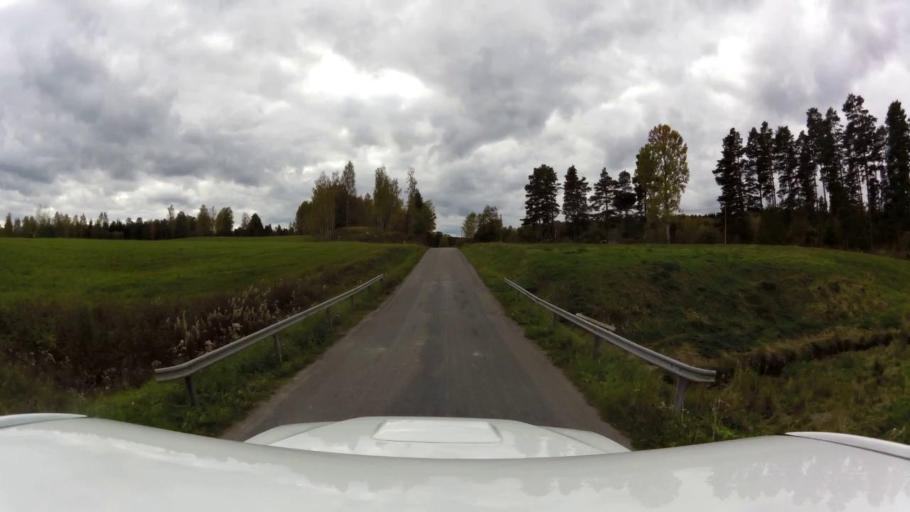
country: SE
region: OEstergoetland
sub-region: Kinda Kommun
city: Rimforsa
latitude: 58.1969
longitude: 15.5689
